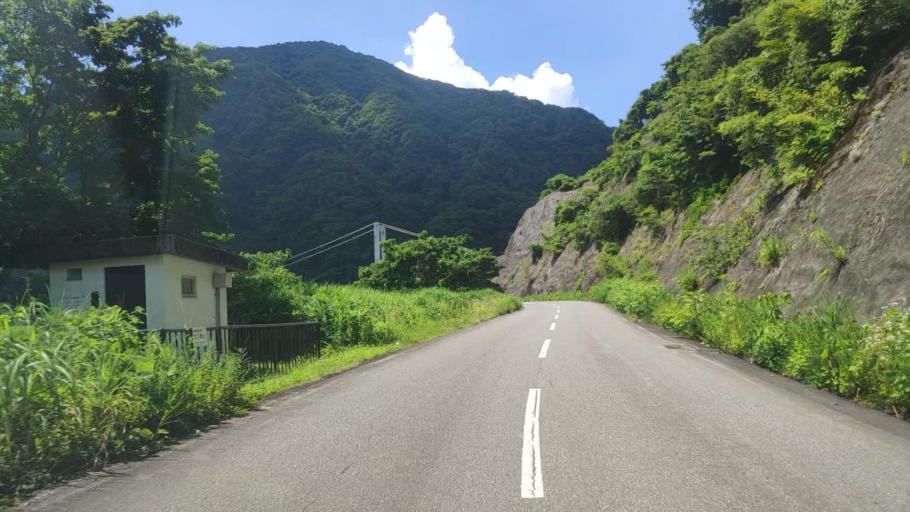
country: JP
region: Fukui
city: Ono
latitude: 35.8974
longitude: 136.5262
